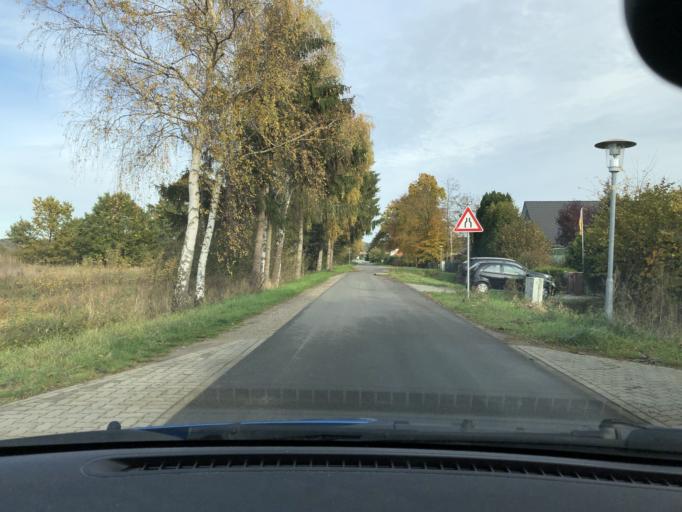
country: DE
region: Lower Saxony
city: Artlenburg
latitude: 53.3703
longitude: 10.4781
